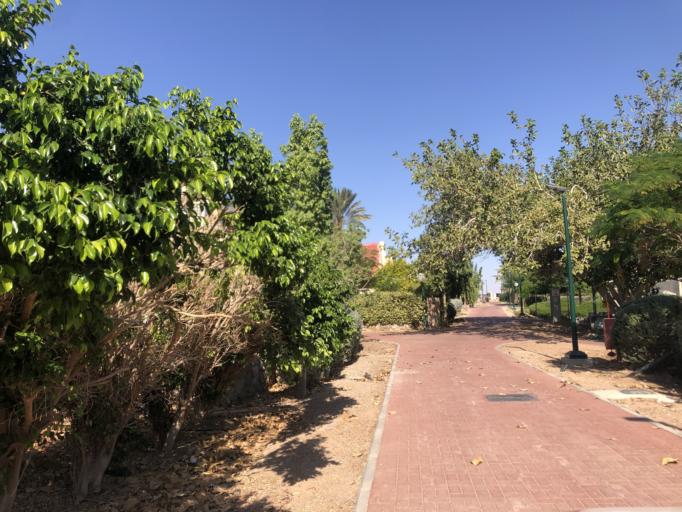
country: IL
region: Southern District
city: Eilat
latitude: 29.5823
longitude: 34.9606
